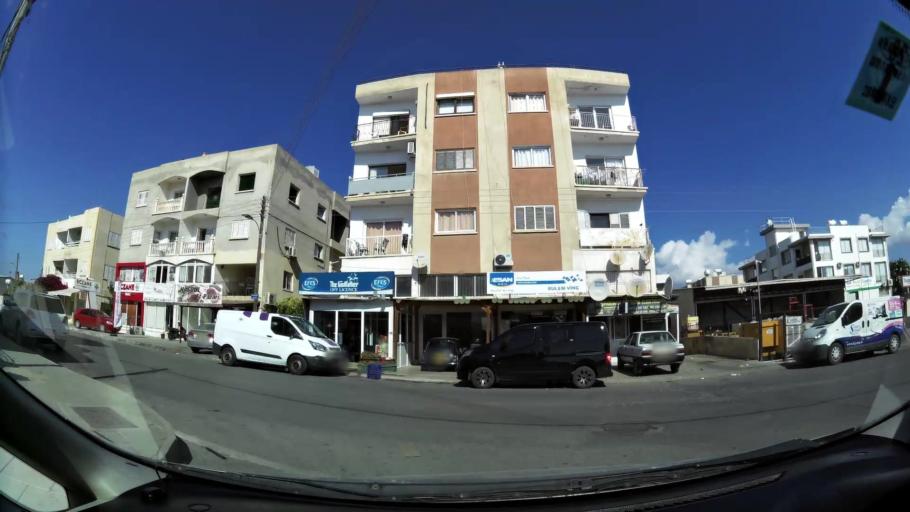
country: CY
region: Lefkosia
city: Nicosia
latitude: 35.2066
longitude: 33.3380
